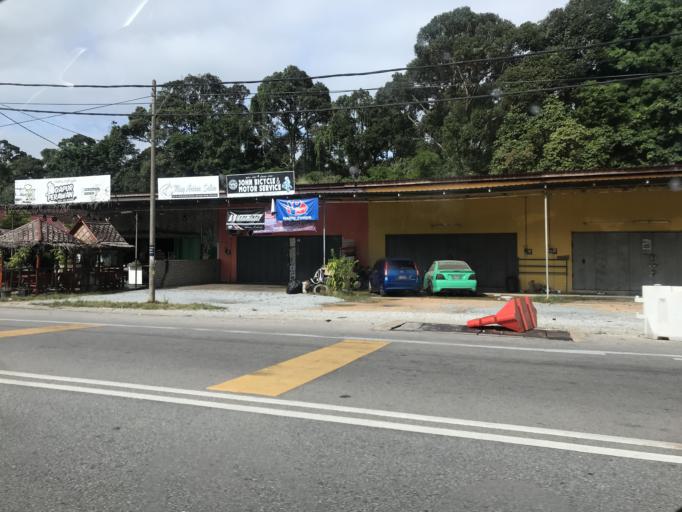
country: MY
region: Kelantan
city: Kota Bharu
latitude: 6.1310
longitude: 102.1775
